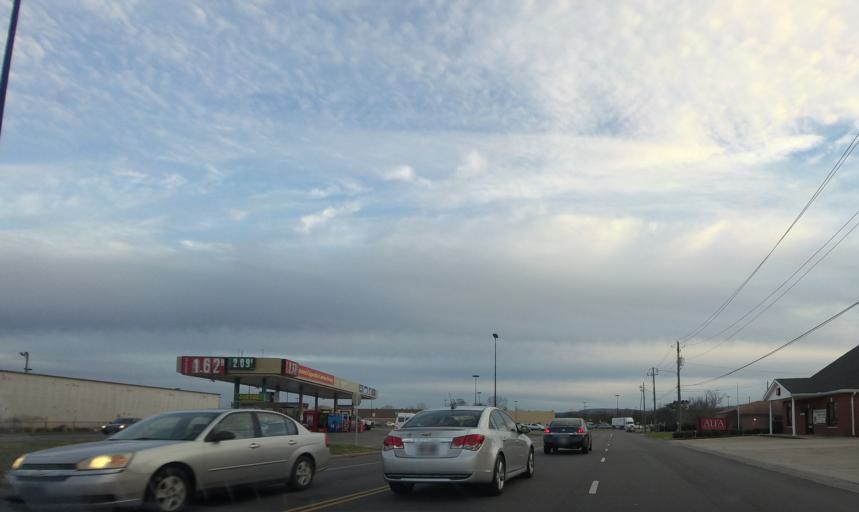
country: US
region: Alabama
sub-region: Calhoun County
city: Oxford
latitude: 33.6009
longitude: -85.8349
